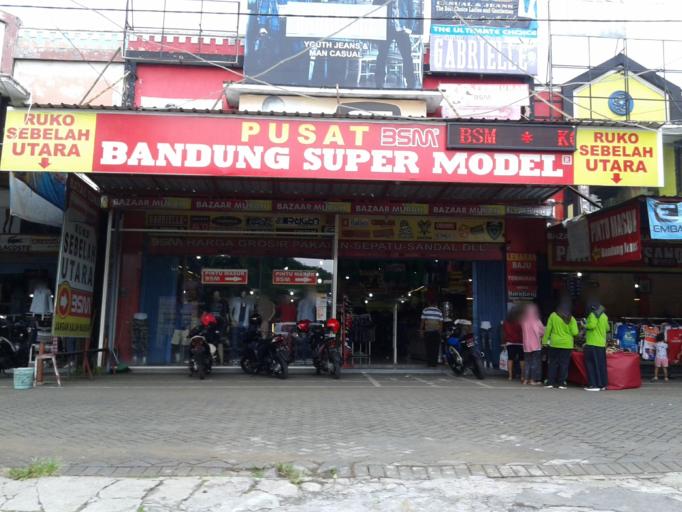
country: ID
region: East Java
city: Singosari
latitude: -7.8794
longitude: 112.6748
